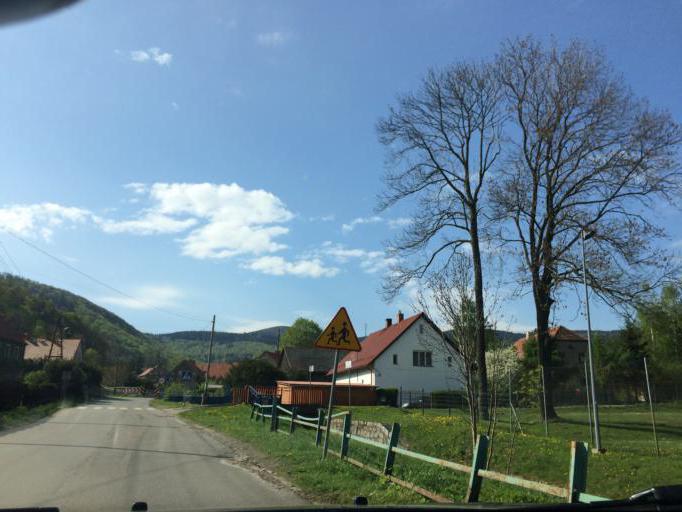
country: PL
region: Lower Silesian Voivodeship
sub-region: Powiat dzierzoniowski
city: Pieszyce
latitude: 50.6806
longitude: 16.5434
